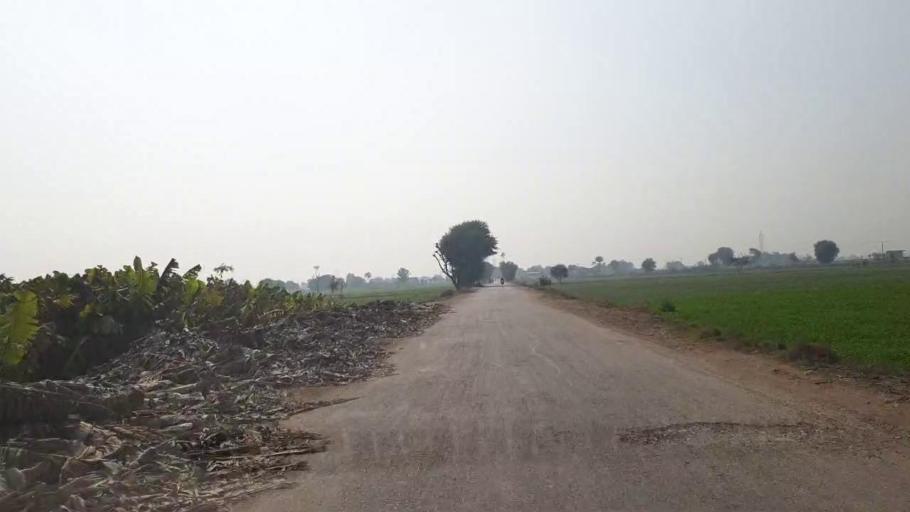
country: PK
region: Sindh
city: Hala
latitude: 25.8516
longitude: 68.4196
